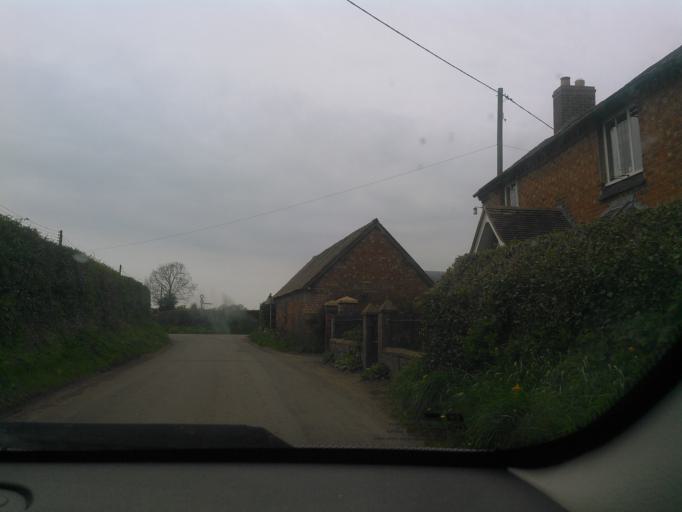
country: GB
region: England
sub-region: Telford and Wrekin
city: Eyton upon the Weald Moors
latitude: 52.7867
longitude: -2.5589
